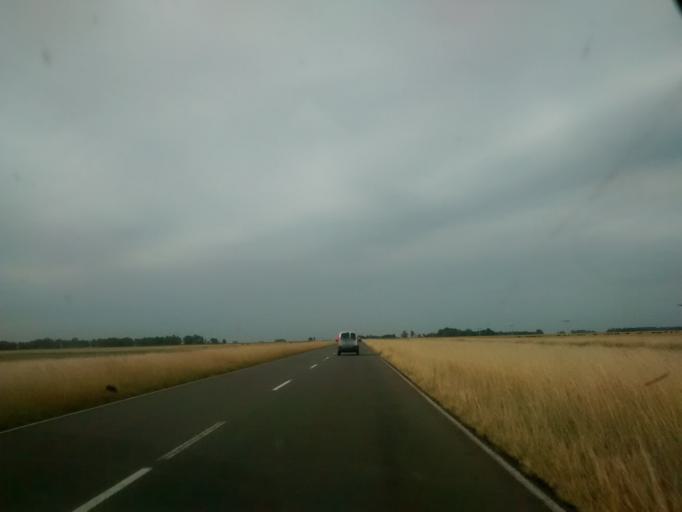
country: AR
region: Buenos Aires
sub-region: Partido de Rauch
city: Rauch
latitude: -36.6159
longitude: -58.5715
